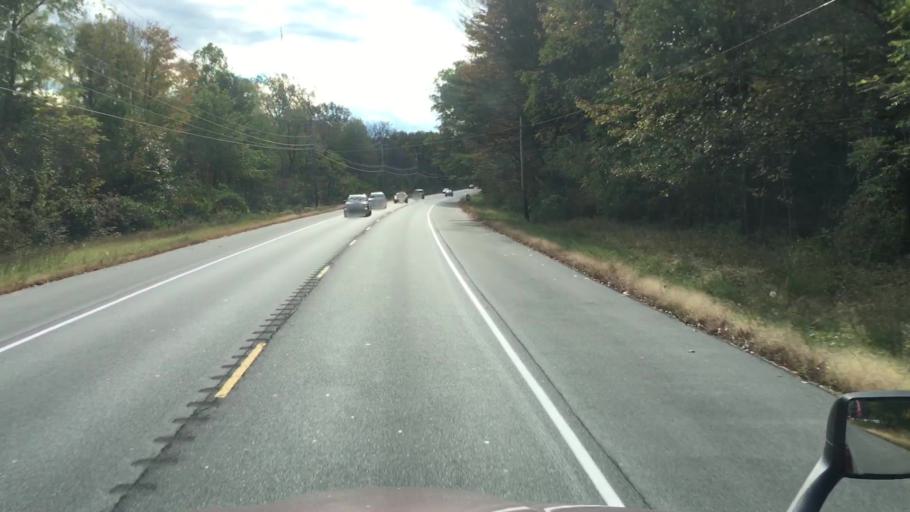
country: US
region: New York
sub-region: Saratoga County
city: Milton
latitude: 43.0290
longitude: -73.8319
